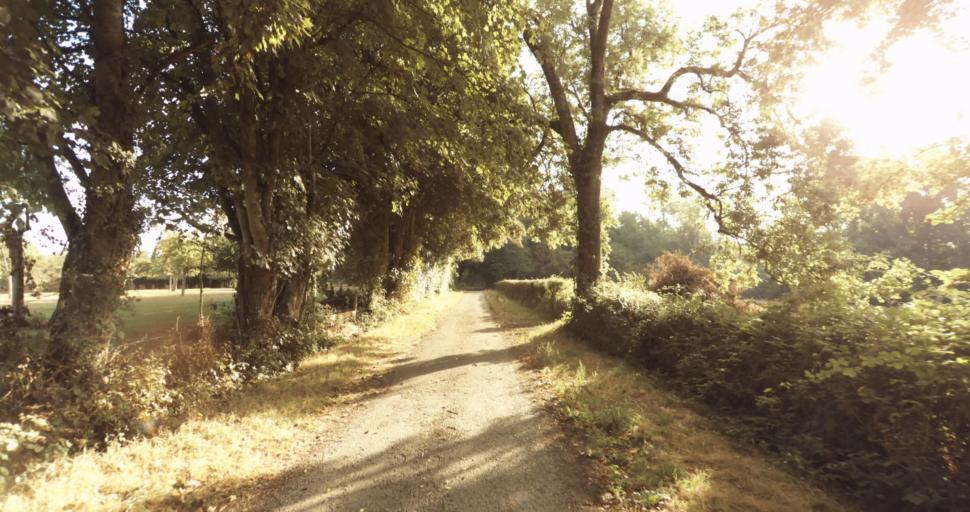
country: FR
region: Lower Normandy
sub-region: Departement de l'Orne
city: Vimoutiers
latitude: 48.9404
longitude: 0.2592
